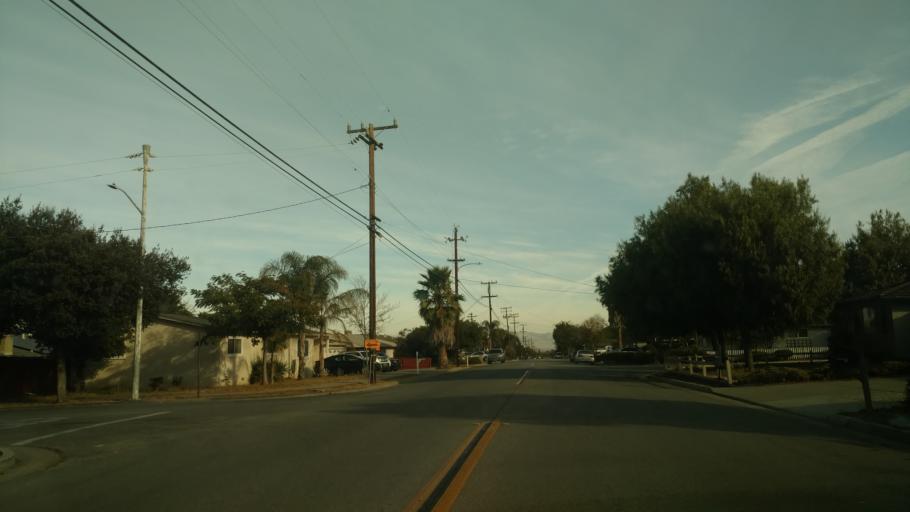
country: US
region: California
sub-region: San Benito County
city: Ridgemark
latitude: 36.8323
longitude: -121.3815
